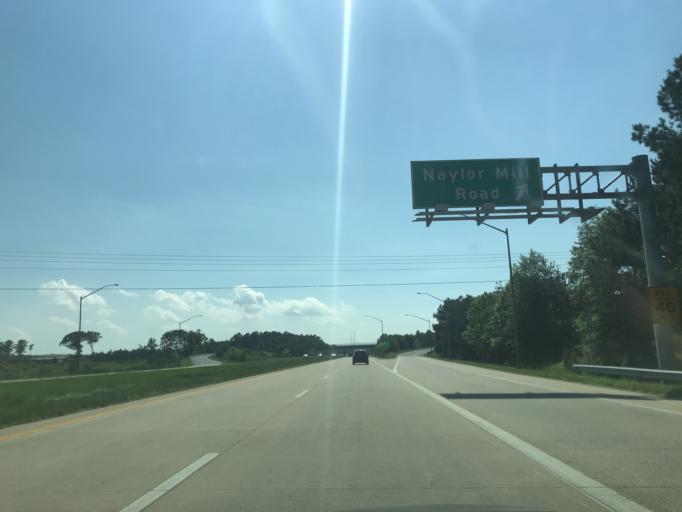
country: US
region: Maryland
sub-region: Wicomico County
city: Salisbury
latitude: 38.4030
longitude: -75.6150
